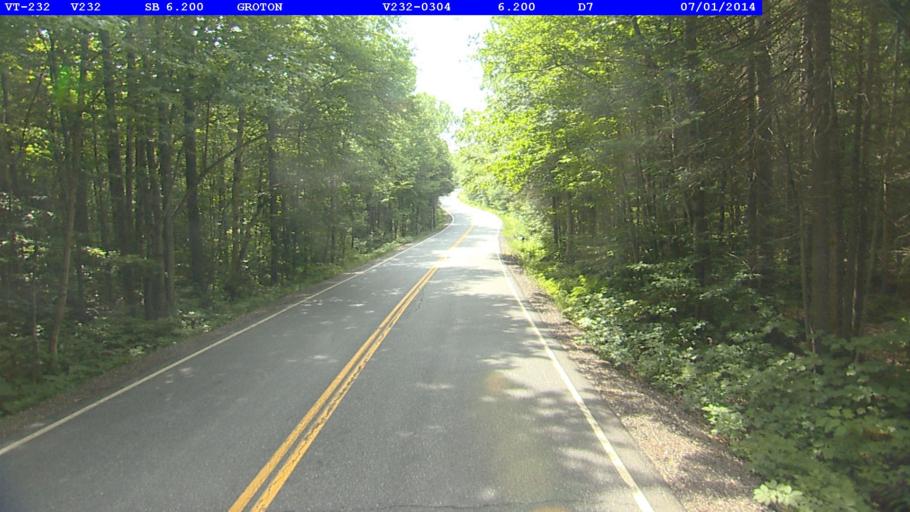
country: US
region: Vermont
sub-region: Washington County
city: Barre
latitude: 44.2849
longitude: -72.2959
